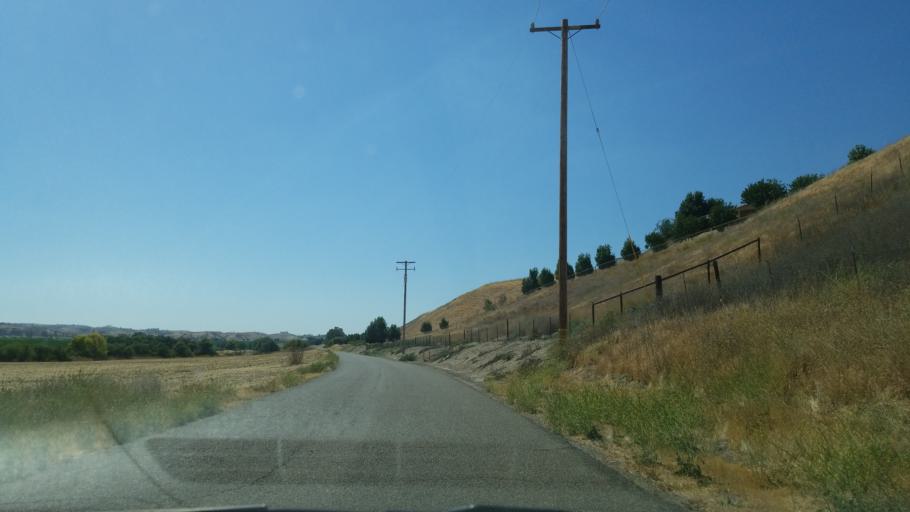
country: US
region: California
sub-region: San Luis Obispo County
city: San Miguel
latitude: 35.7311
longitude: -120.6583
